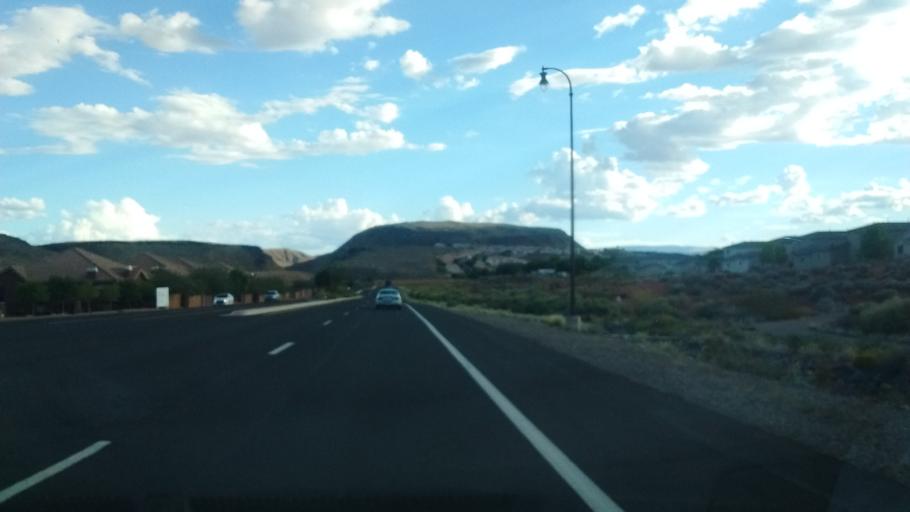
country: US
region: Utah
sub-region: Washington County
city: Washington
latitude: 37.1378
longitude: -113.4858
